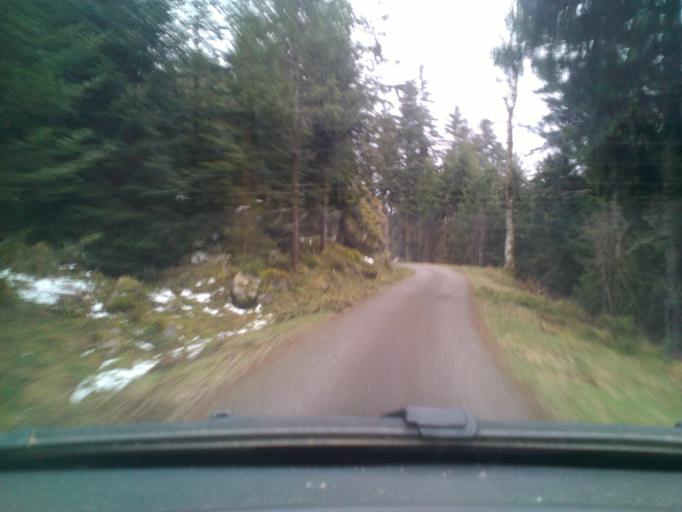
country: FR
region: Lorraine
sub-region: Departement des Vosges
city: Gerardmer
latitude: 48.1089
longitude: 6.8727
